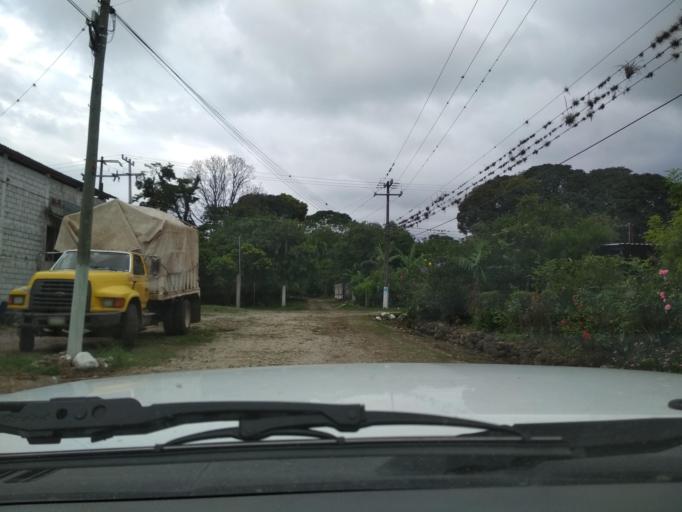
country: MX
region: Veracruz
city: Paraje Nuevo
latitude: 18.8736
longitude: -96.8808
